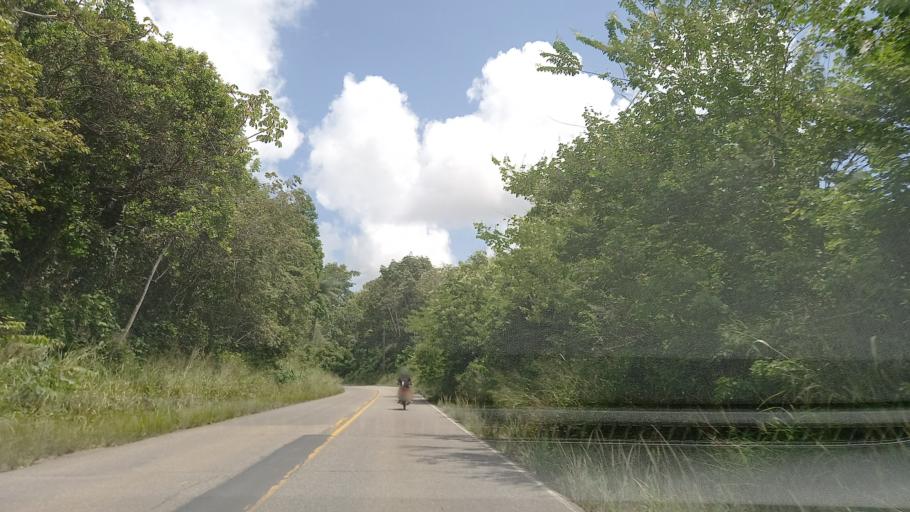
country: BR
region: Pernambuco
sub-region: Rio Formoso
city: Rio Formoso
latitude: -8.6480
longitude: -35.1297
